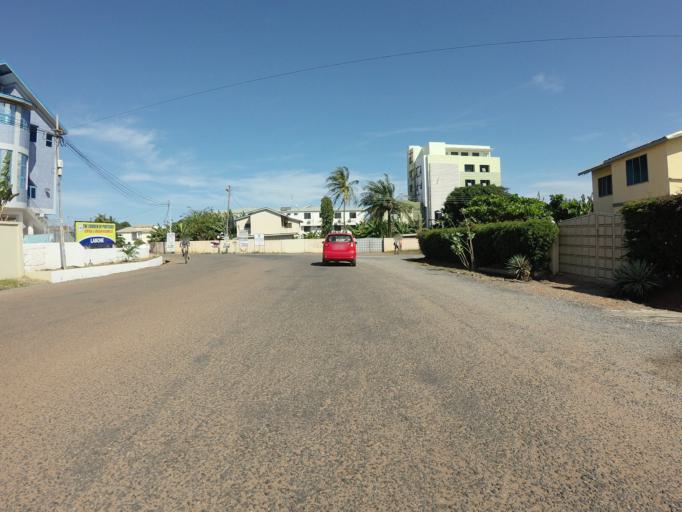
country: GH
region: Greater Accra
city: Accra
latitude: 5.5618
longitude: -0.1683
